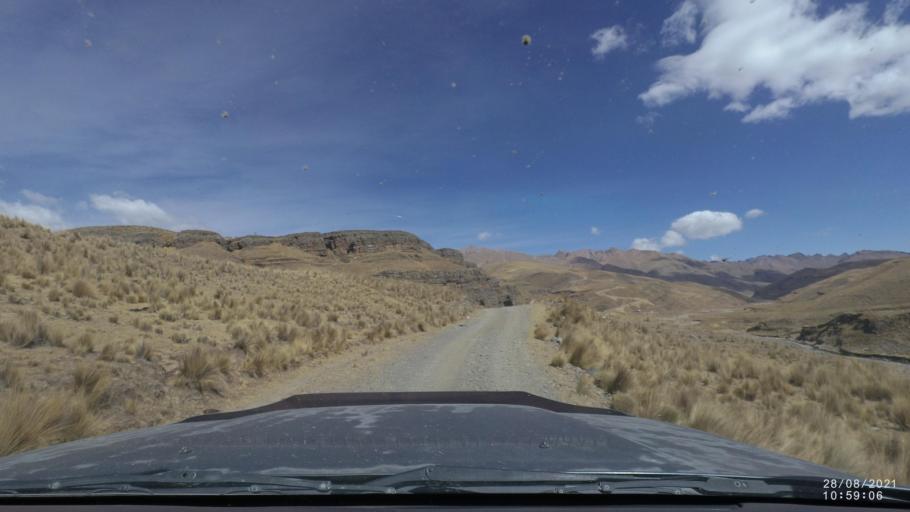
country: BO
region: Cochabamba
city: Cochabamba
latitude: -17.1831
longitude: -66.2556
